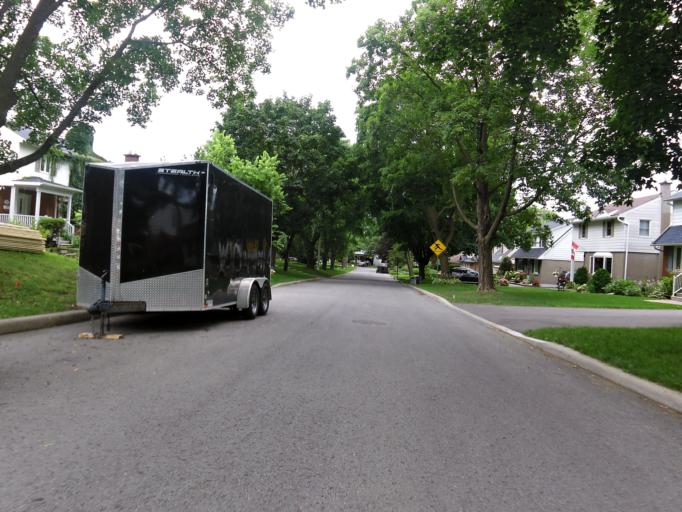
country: CA
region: Ontario
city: Ottawa
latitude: 45.3886
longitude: -75.6675
